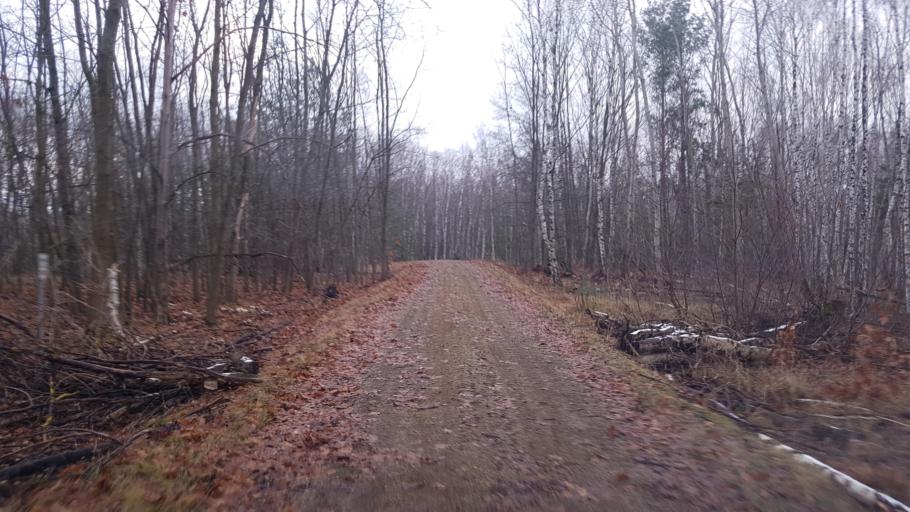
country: DE
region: Brandenburg
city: Plessa
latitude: 51.5198
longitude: 13.6825
